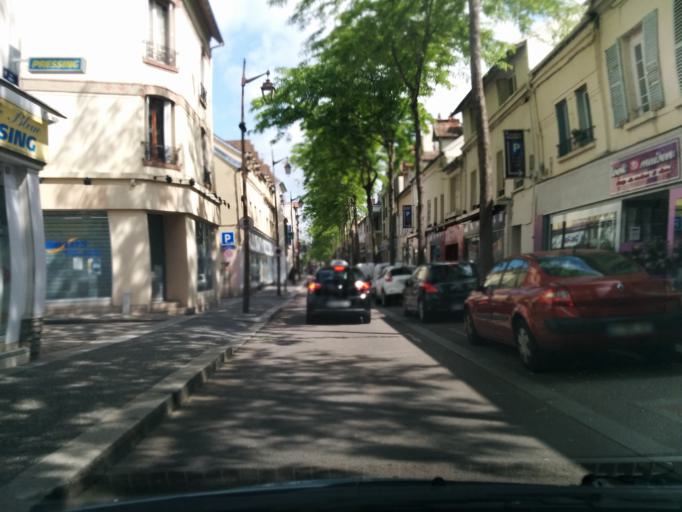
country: FR
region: Ile-de-France
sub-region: Departement des Yvelines
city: Mantes-la-Jolie
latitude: 48.9871
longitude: 1.7174
